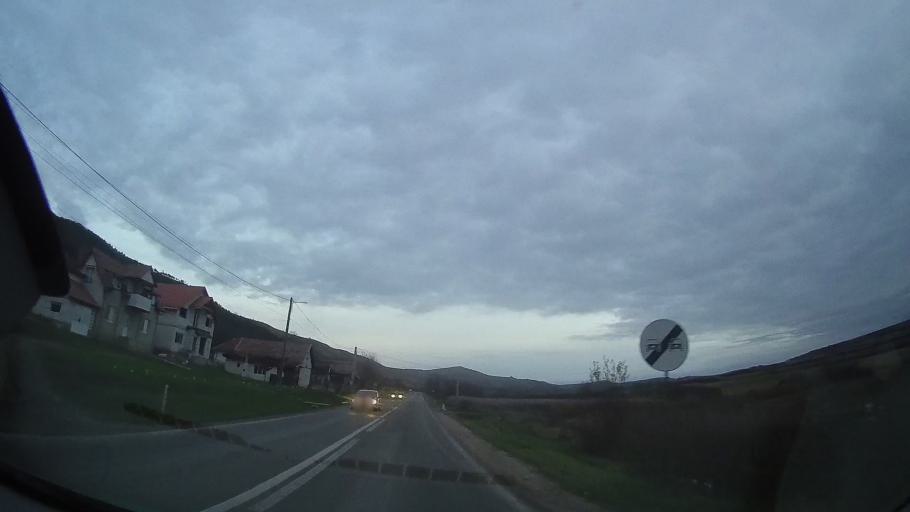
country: RO
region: Cluj
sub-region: Comuna Caianu
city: Caianu
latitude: 46.8020
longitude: 23.9313
